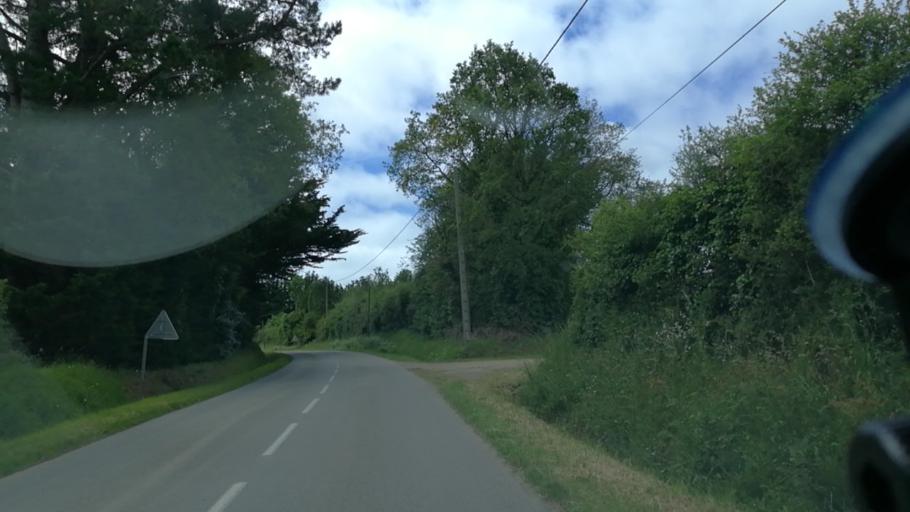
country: FR
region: Brittany
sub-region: Departement du Morbihan
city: Penestin
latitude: 47.4884
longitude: -2.4367
